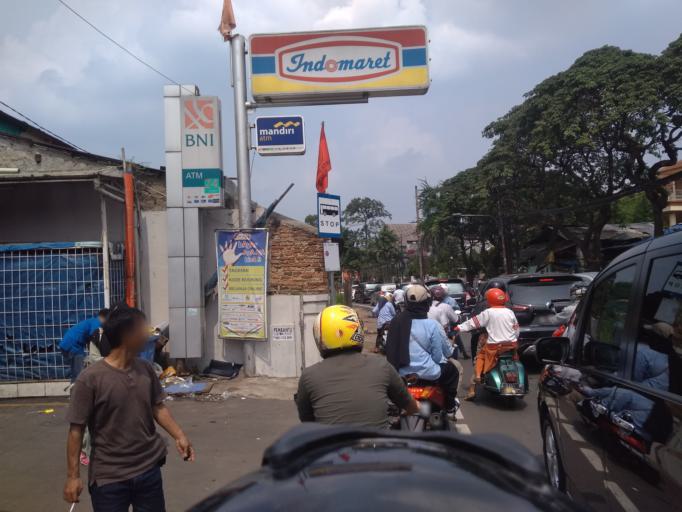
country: ID
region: Banten
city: South Tangerang
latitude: -6.2902
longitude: 106.7709
